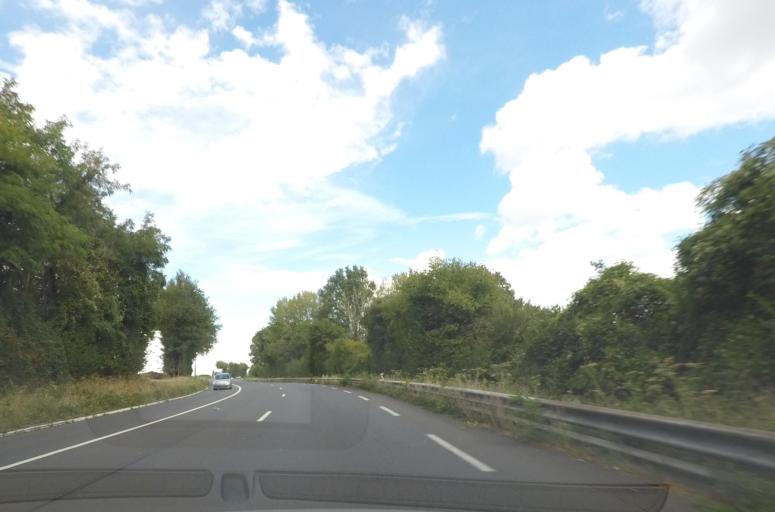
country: FR
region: Pays de la Loire
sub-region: Departement de la Sarthe
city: Clermont-Creans
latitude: 47.7276
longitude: -0.0099
